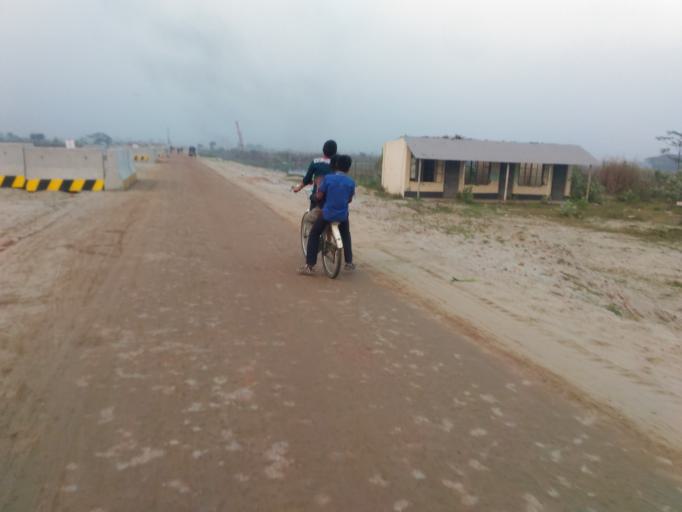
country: BD
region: Dhaka
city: Tungi
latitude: 23.8497
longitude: 90.3635
